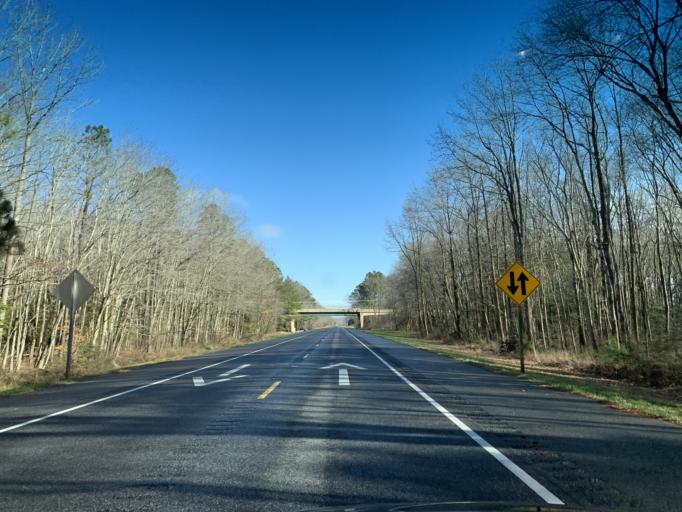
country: US
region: Maryland
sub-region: Worcester County
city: Berlin
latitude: 38.3730
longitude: -75.2547
